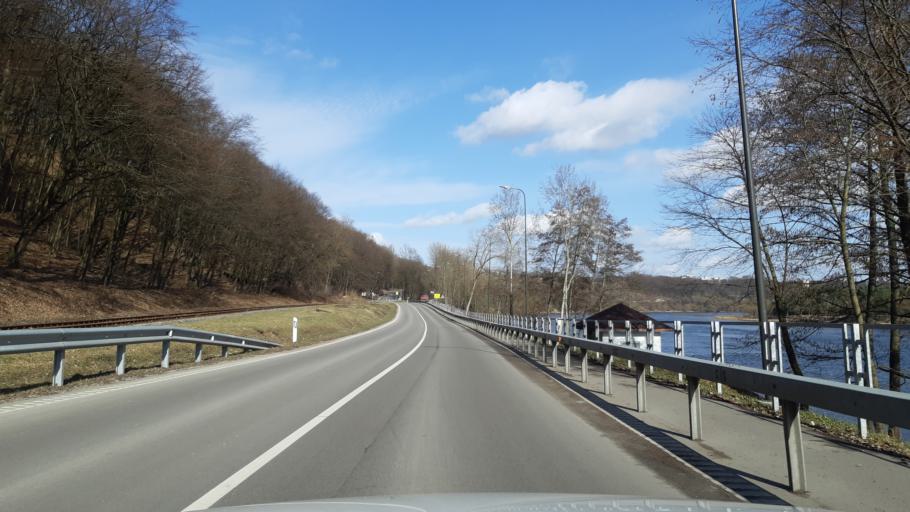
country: LT
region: Kauno apskritis
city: Dainava (Kaunas)
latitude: 54.8850
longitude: 23.9561
